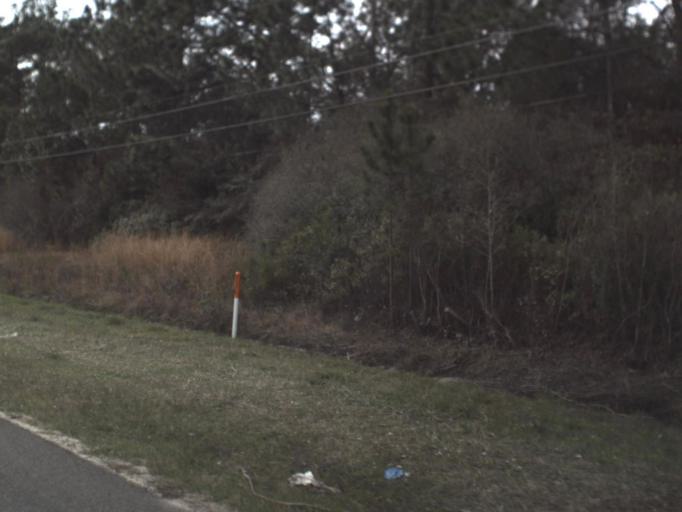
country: US
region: Florida
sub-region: Bay County
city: Hiland Park
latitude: 30.2123
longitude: -85.6089
